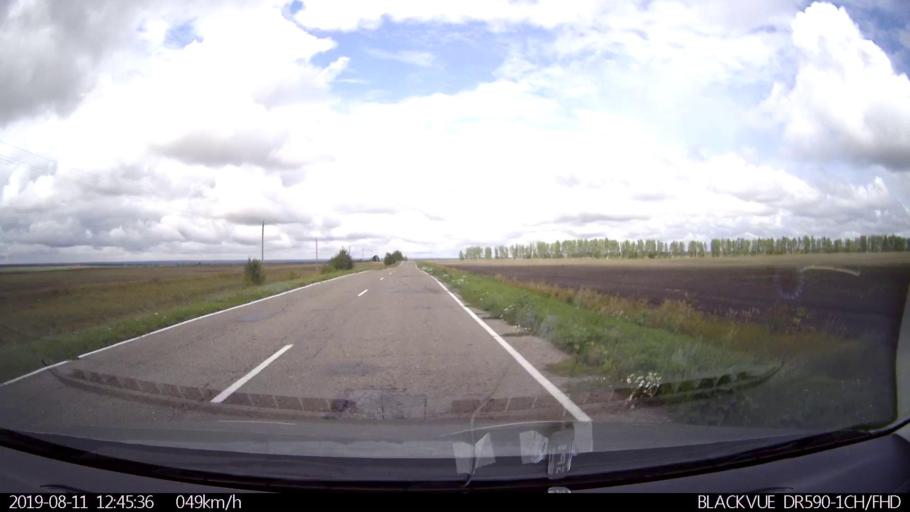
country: RU
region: Ulyanovsk
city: Ignatovka
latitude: 53.8602
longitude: 47.7265
